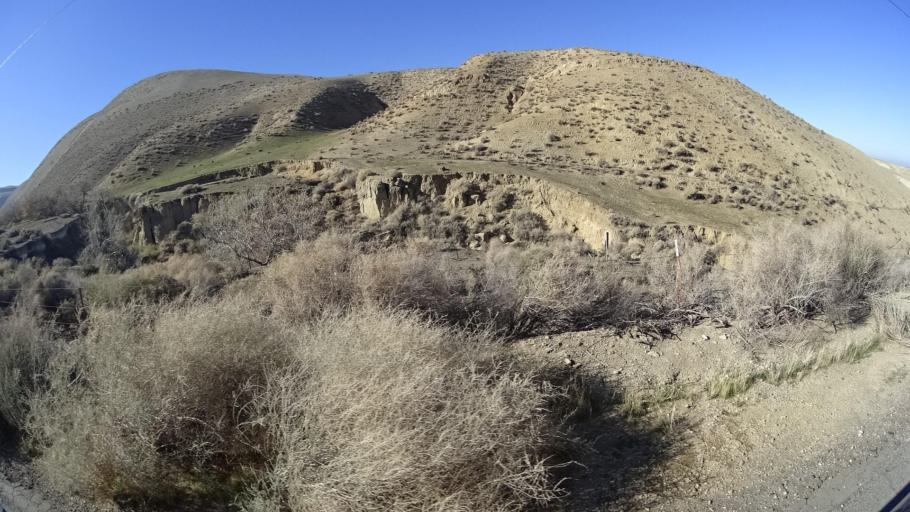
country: US
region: California
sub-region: Kern County
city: Maricopa
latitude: 34.9808
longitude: -119.4007
